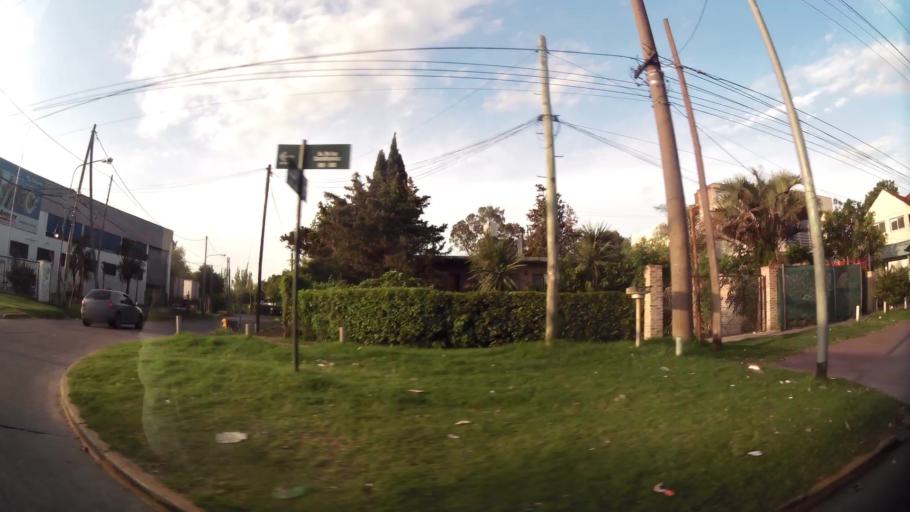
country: AR
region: Buenos Aires
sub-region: Partido de Tigre
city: Tigre
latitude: -34.4536
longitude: -58.6445
